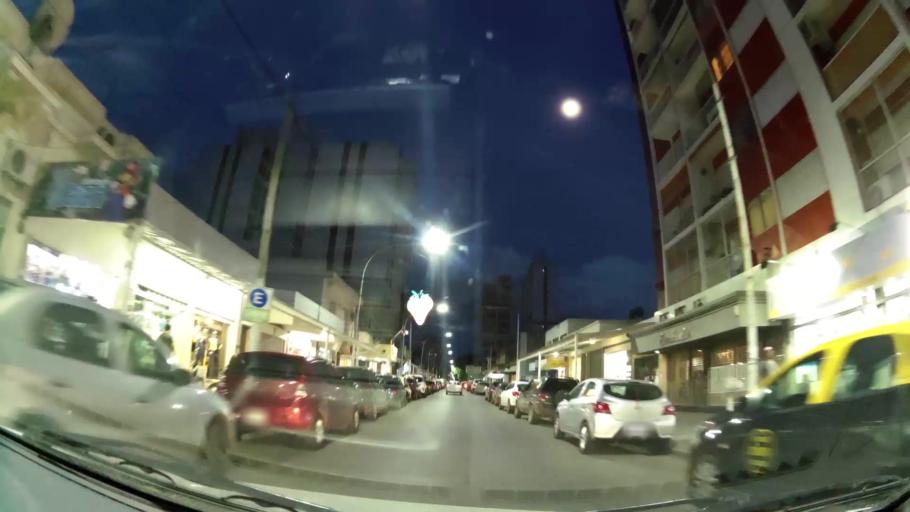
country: AR
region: Buenos Aires
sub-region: Partido de Quilmes
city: Quilmes
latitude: -34.6994
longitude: -58.3121
